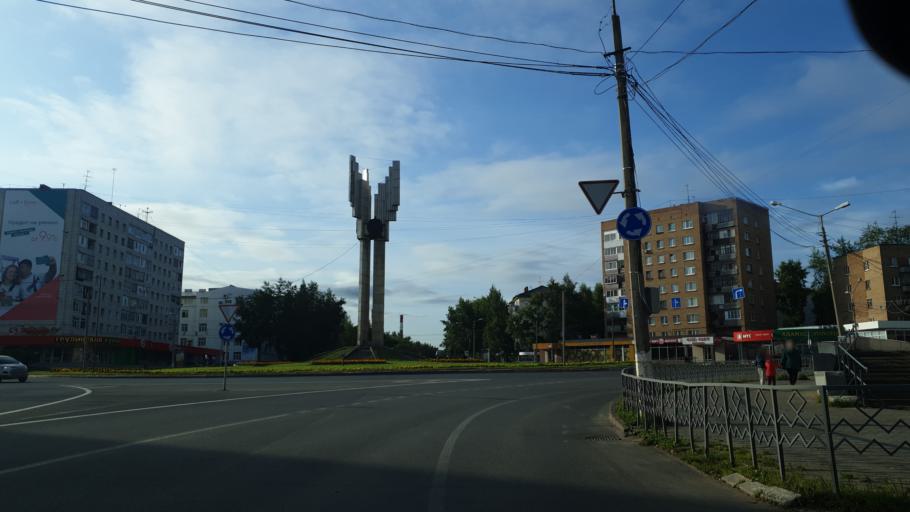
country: RU
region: Komi Republic
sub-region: Syktyvdinskiy Rayon
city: Syktyvkar
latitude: 61.6633
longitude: 50.8167
